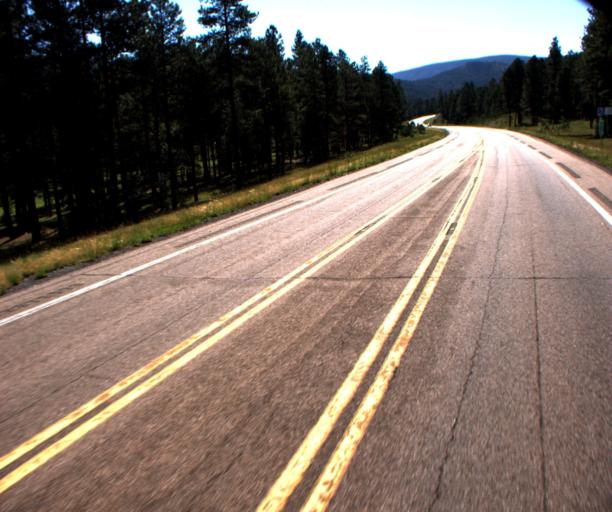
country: US
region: Arizona
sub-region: Apache County
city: Eagar
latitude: 33.9414
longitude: -109.1991
